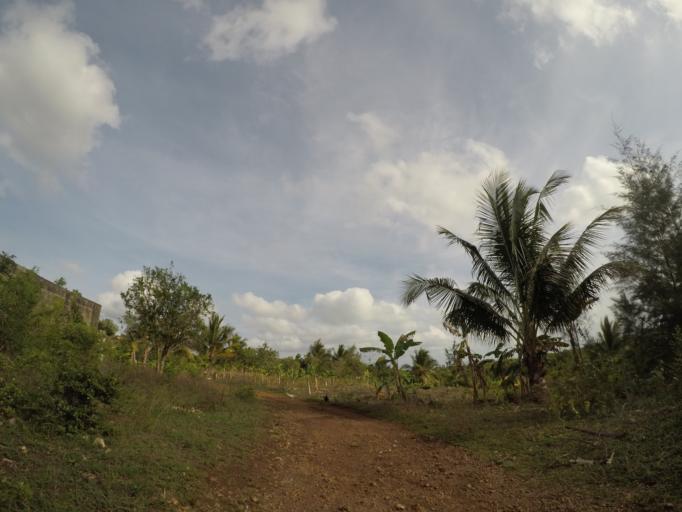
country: TZ
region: Zanzibar Central/South
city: Koani
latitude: -6.2281
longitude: 39.3112
